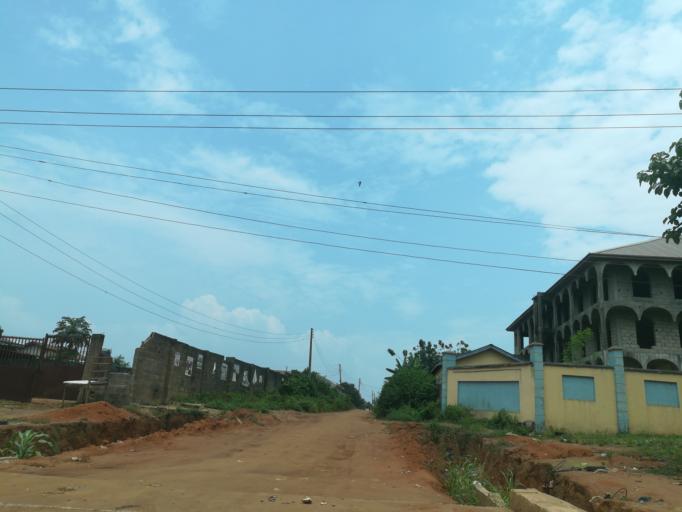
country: NG
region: Lagos
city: Ikorodu
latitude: 6.5842
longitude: 3.5874
